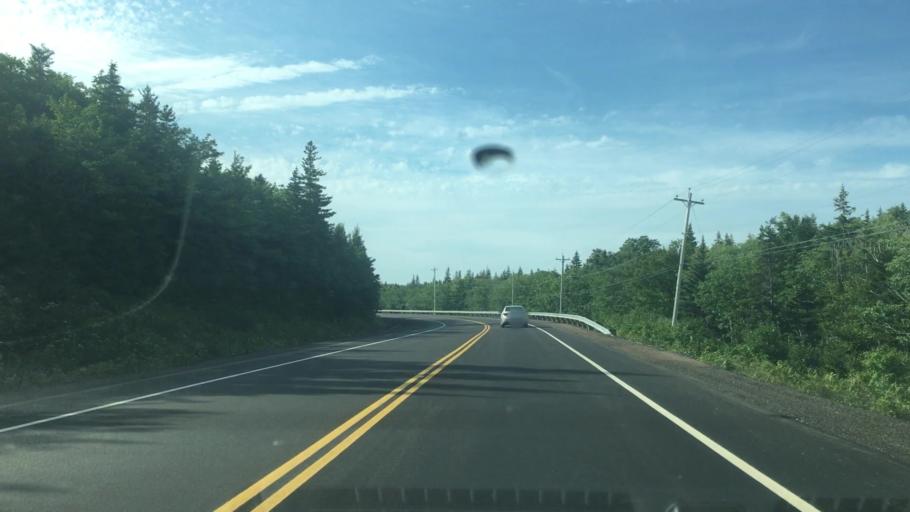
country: CA
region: Nova Scotia
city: Sydney Mines
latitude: 46.8390
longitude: -60.3870
